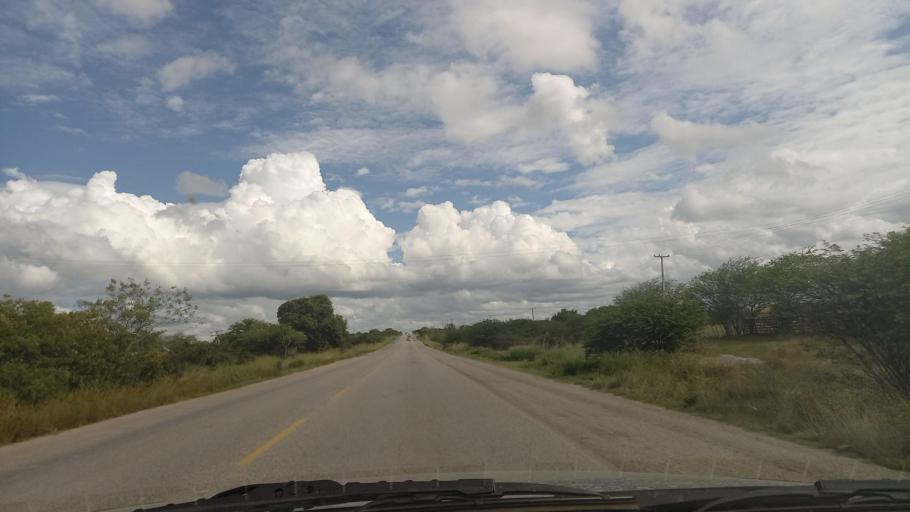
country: BR
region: Pernambuco
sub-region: Cachoeirinha
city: Cachoeirinha
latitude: -8.4365
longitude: -36.2032
